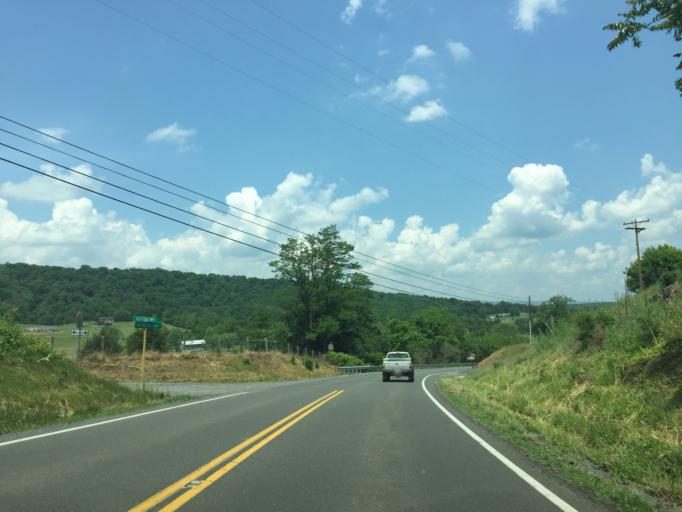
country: US
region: Virginia
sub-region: Shenandoah County
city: Strasburg
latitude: 39.0612
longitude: -78.3724
